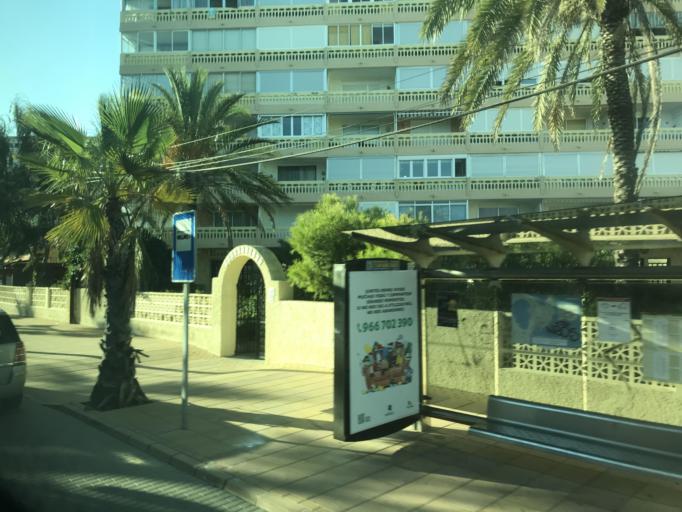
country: ES
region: Valencia
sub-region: Provincia de Alicante
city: Torrevieja
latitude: 38.0205
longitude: -0.6551
